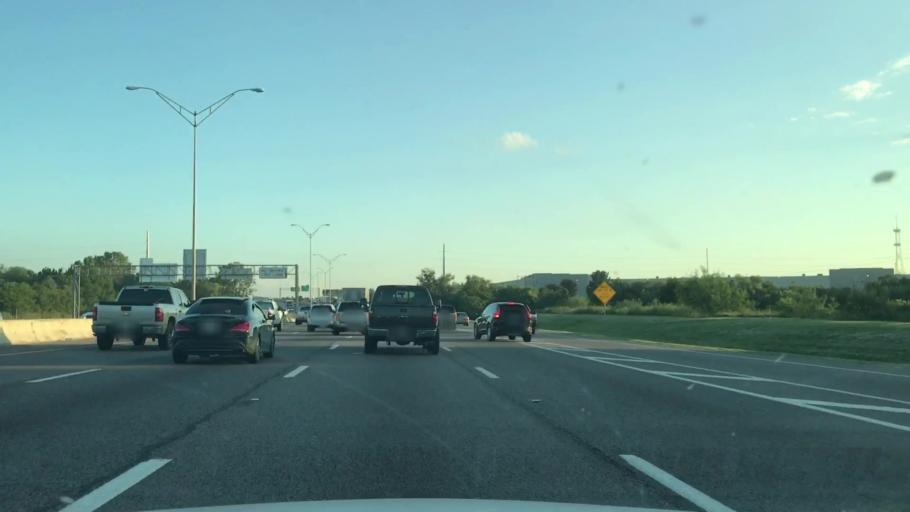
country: US
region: Texas
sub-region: Dallas County
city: Mesquite
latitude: 32.7779
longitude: -96.6244
